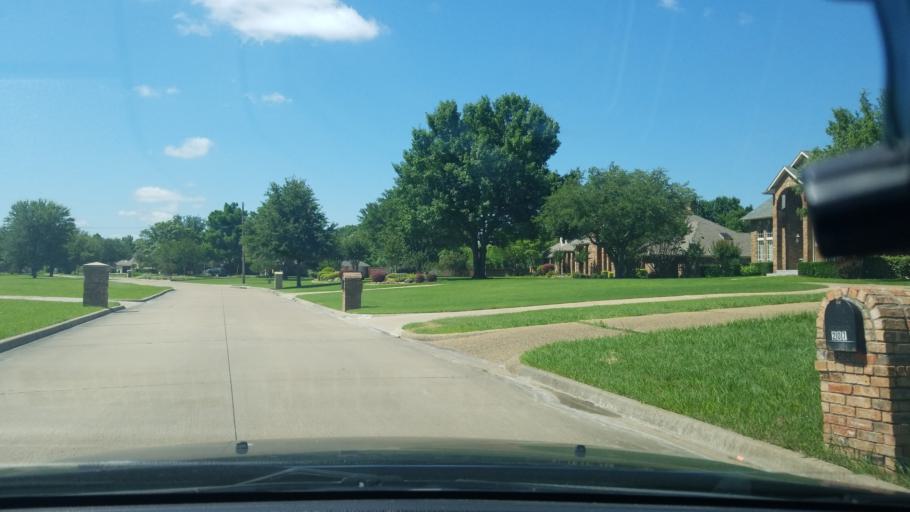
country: US
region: Texas
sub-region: Dallas County
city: Sunnyvale
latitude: 32.7999
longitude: -96.5926
